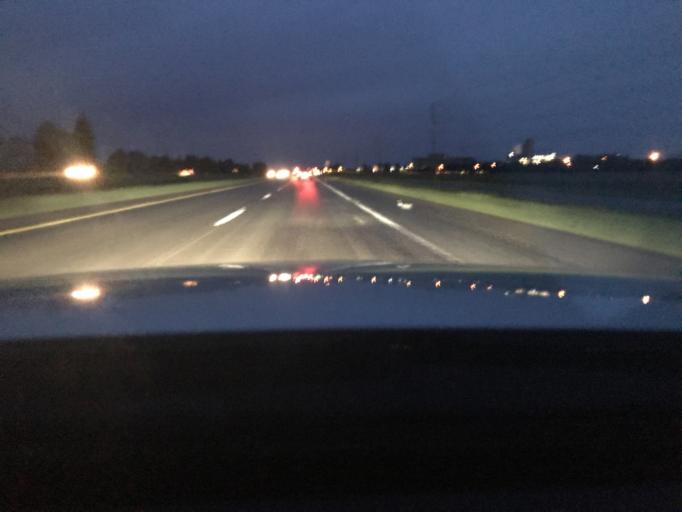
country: US
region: Colorado
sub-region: Larimer County
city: Wellington
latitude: 40.6313
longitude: -105.0013
